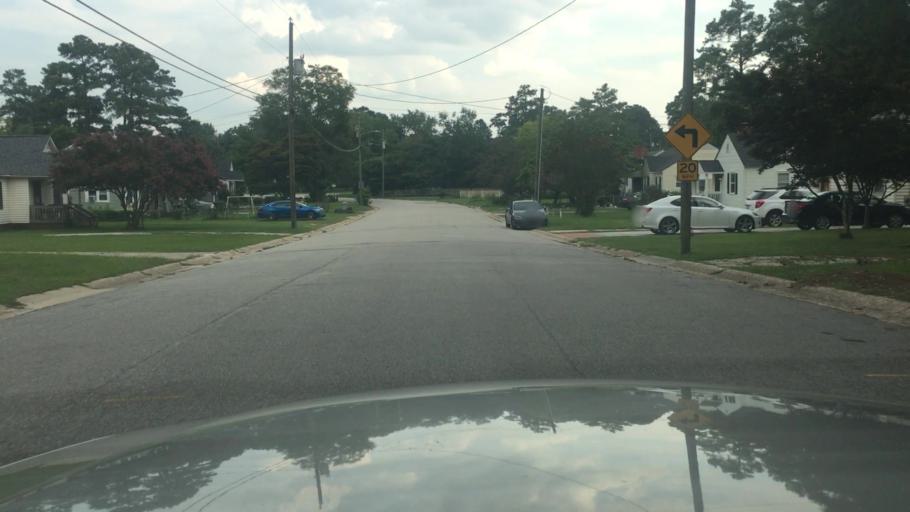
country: US
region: North Carolina
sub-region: Cumberland County
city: Fayetteville
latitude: 35.0724
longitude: -78.9167
